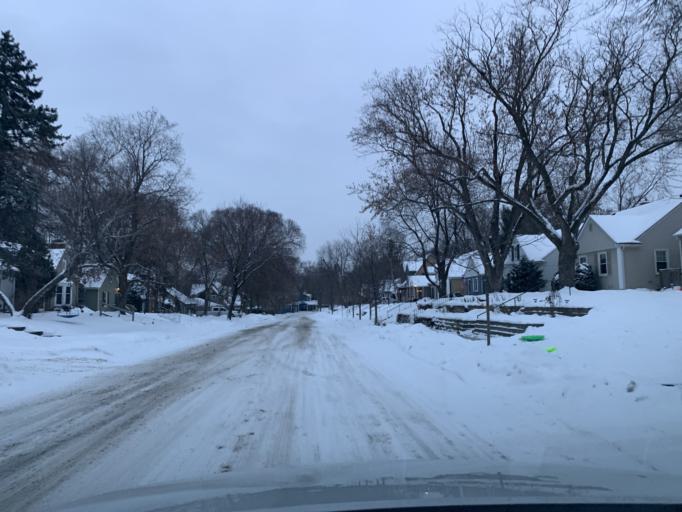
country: US
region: Minnesota
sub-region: Hennepin County
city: Saint Louis Park
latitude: 44.9251
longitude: -93.3456
